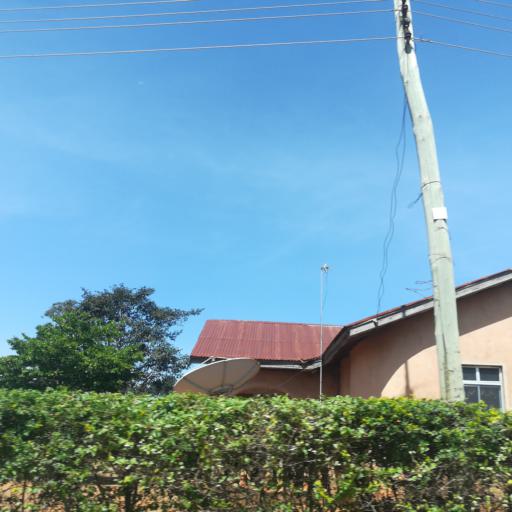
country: NG
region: Plateau
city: Bukuru
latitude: 9.7600
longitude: 8.8798
